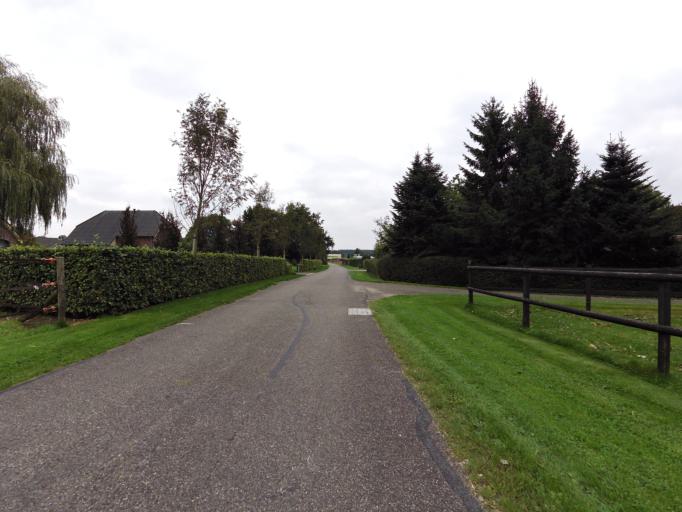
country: NL
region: Gelderland
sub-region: Gemeente Montferland
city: s-Heerenberg
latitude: 51.9139
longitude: 6.1890
